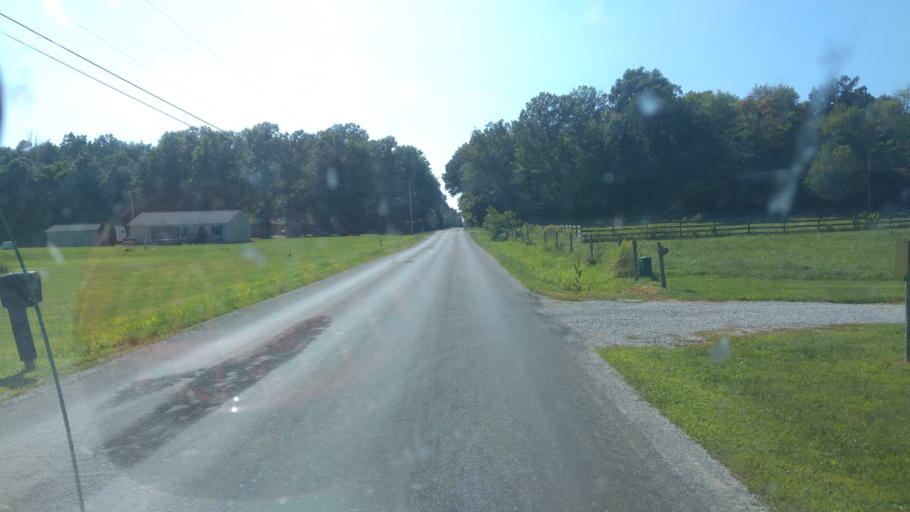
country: US
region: Ohio
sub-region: Ashland County
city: Ashland
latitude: 40.9701
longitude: -82.2901
